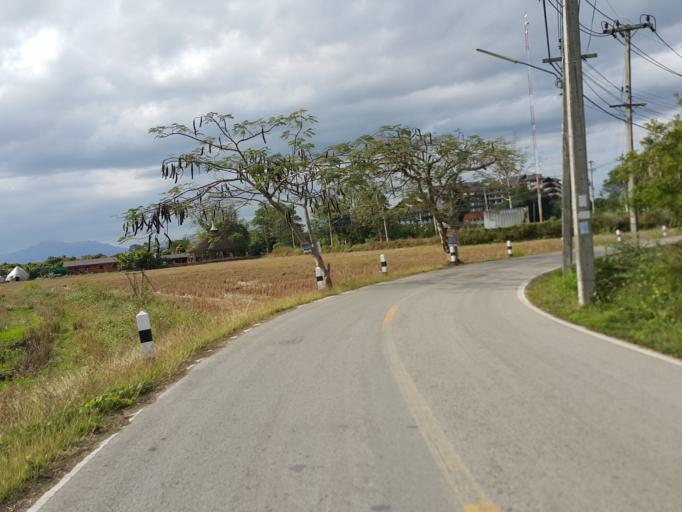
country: TH
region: Chiang Mai
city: San Sai
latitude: 18.8856
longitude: 99.1027
